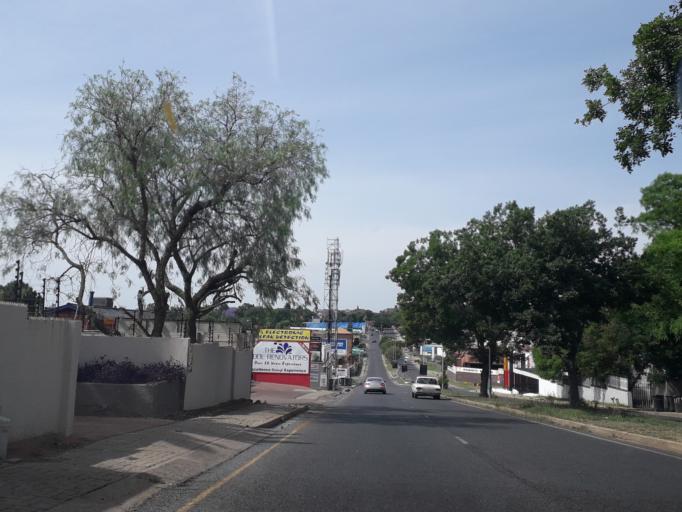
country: ZA
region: Gauteng
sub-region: City of Johannesburg Metropolitan Municipality
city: Roodepoort
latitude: -26.1082
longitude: 27.9744
